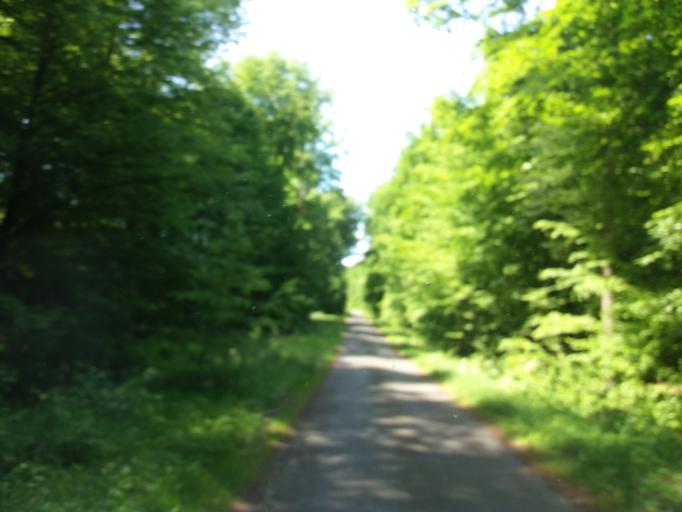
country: PL
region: West Pomeranian Voivodeship
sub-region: Powiat stargardzki
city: Dobrzany
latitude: 53.3506
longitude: 15.4684
